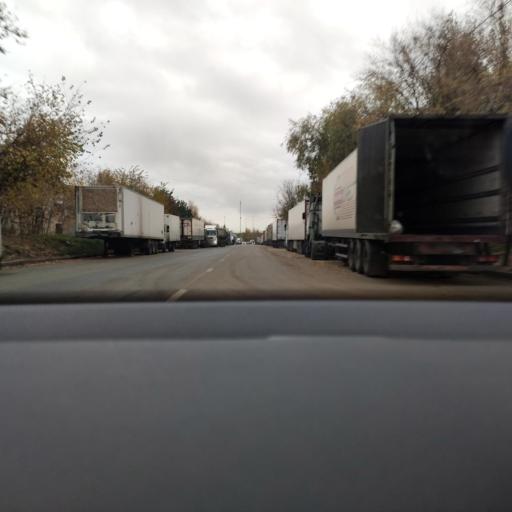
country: RU
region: Moscow
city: Mikhalkovo
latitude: 55.6736
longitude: 37.4302
